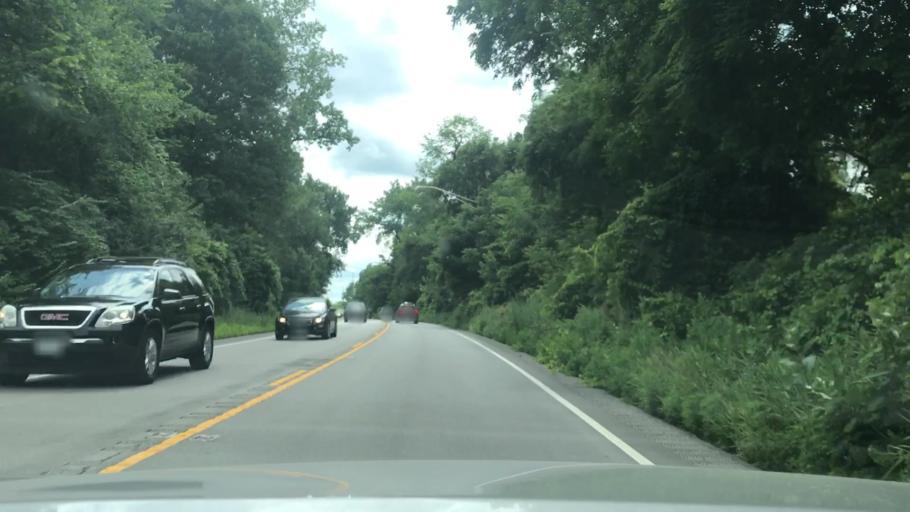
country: US
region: Illinois
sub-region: DuPage County
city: Burr Ridge
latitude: 41.7005
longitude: -87.9325
